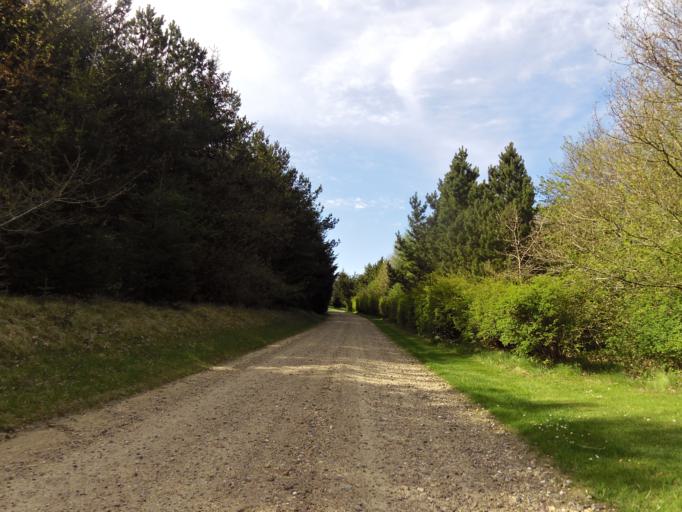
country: DK
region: Central Jutland
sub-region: Holstebro Kommune
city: Vinderup
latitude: 56.4691
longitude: 8.8857
